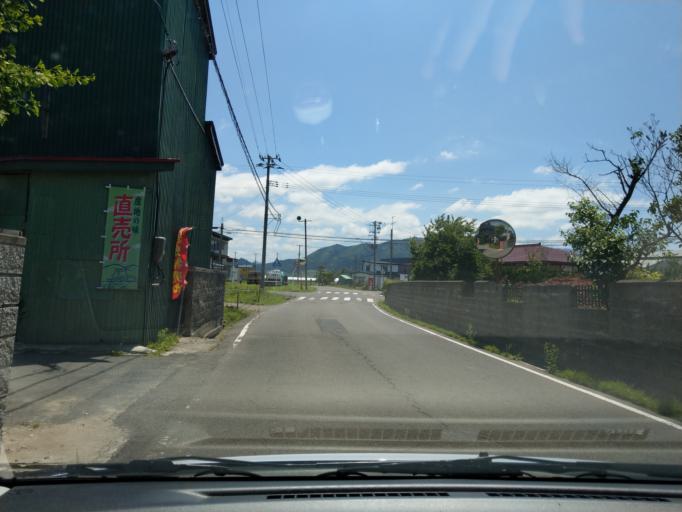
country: JP
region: Aomori
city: Hirosaki
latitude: 40.5659
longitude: 140.5516
